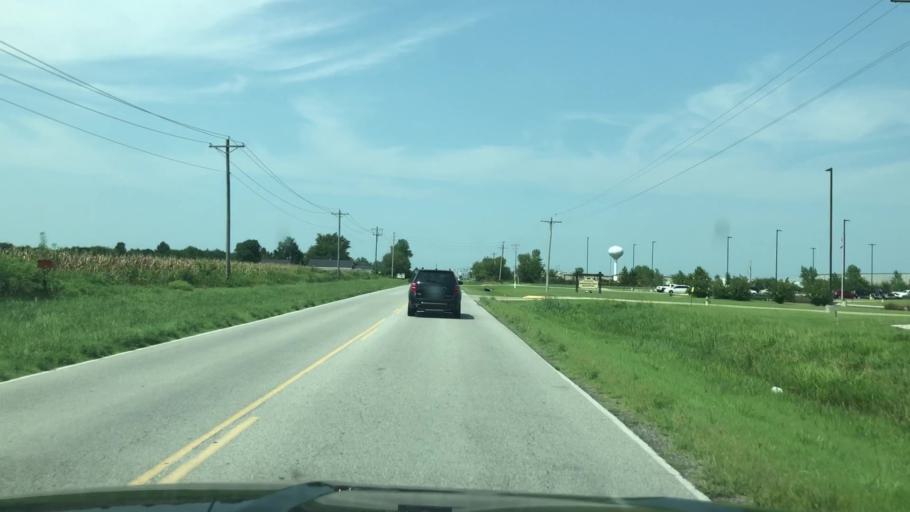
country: US
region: Oklahoma
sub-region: Ottawa County
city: Commerce
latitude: 36.9052
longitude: -94.8419
